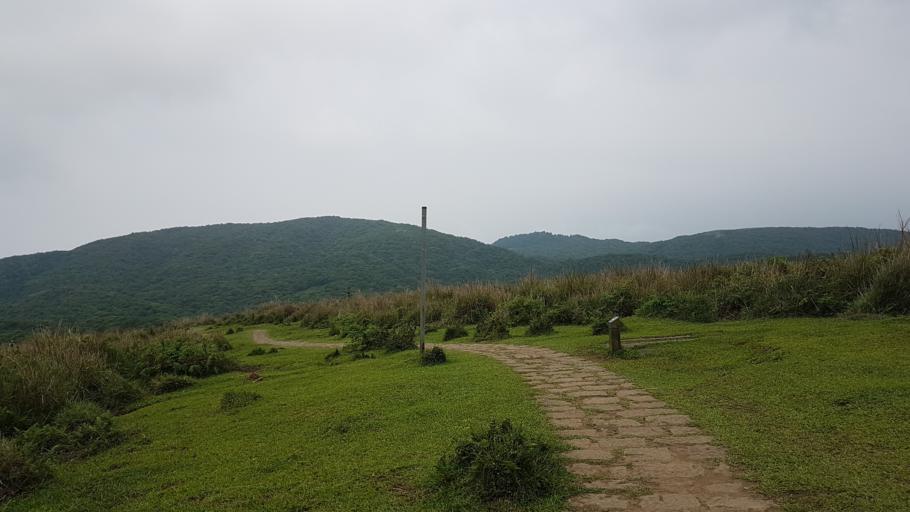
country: TW
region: Taipei
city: Taipei
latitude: 25.1611
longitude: 121.5753
